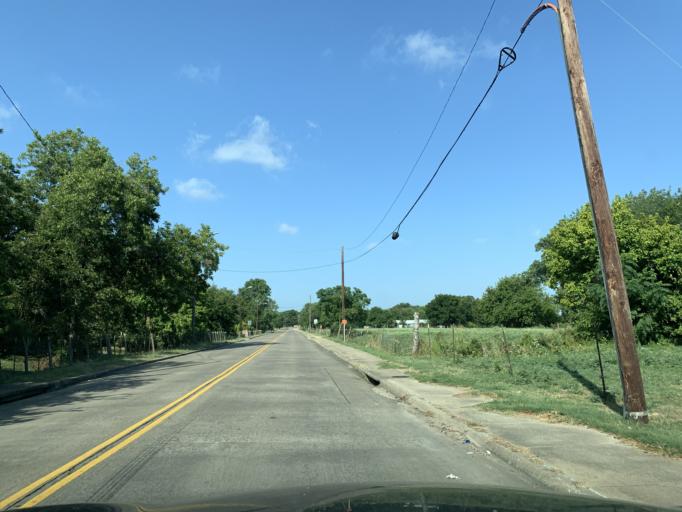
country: US
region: Texas
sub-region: Dallas County
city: Hutchins
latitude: 32.6800
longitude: -96.7886
